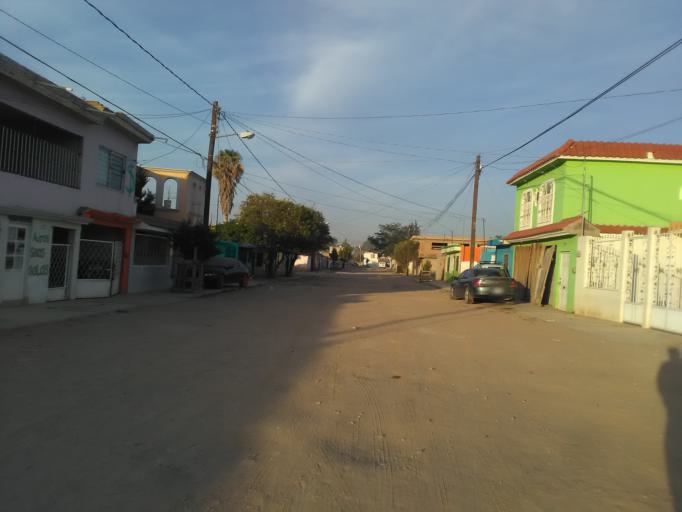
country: MX
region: Durango
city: Victoria de Durango
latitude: 24.0539
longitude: -104.6413
